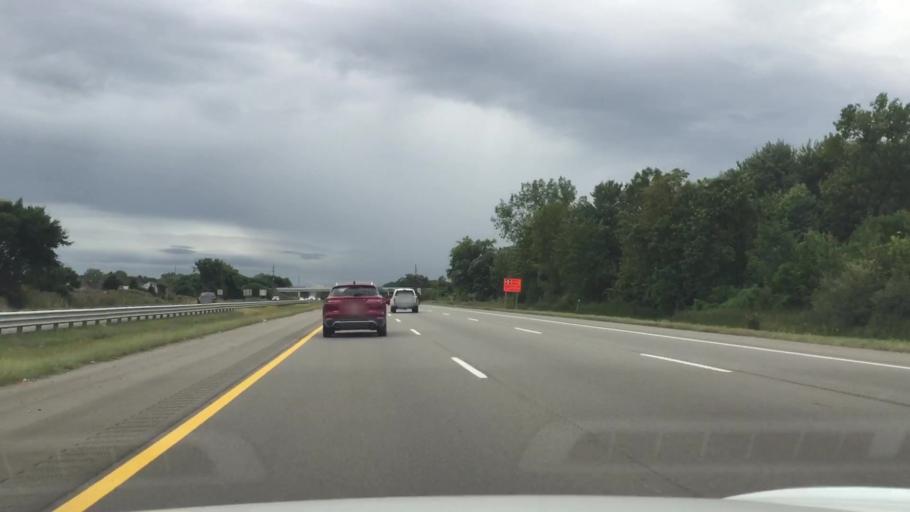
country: US
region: Michigan
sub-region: Macomb County
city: New Haven
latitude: 42.6678
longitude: -82.8270
